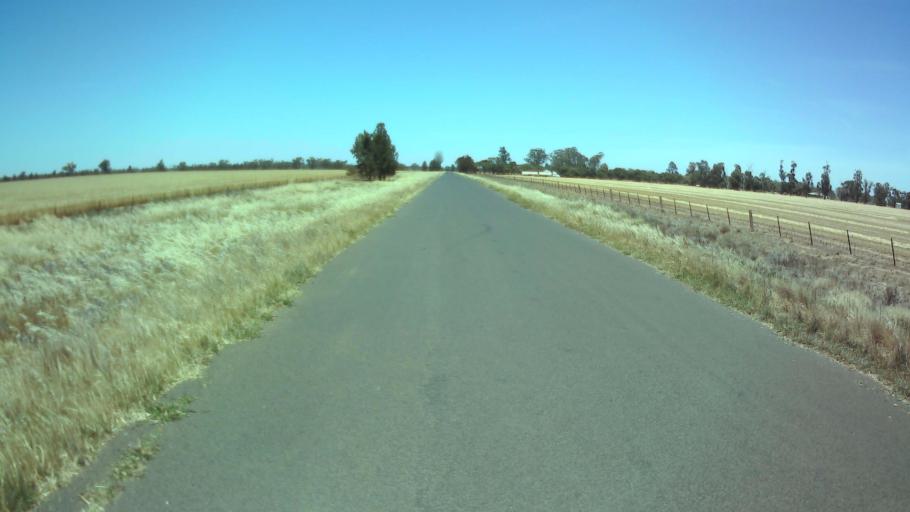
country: AU
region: New South Wales
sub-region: Weddin
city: Grenfell
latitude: -34.0263
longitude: 147.7916
